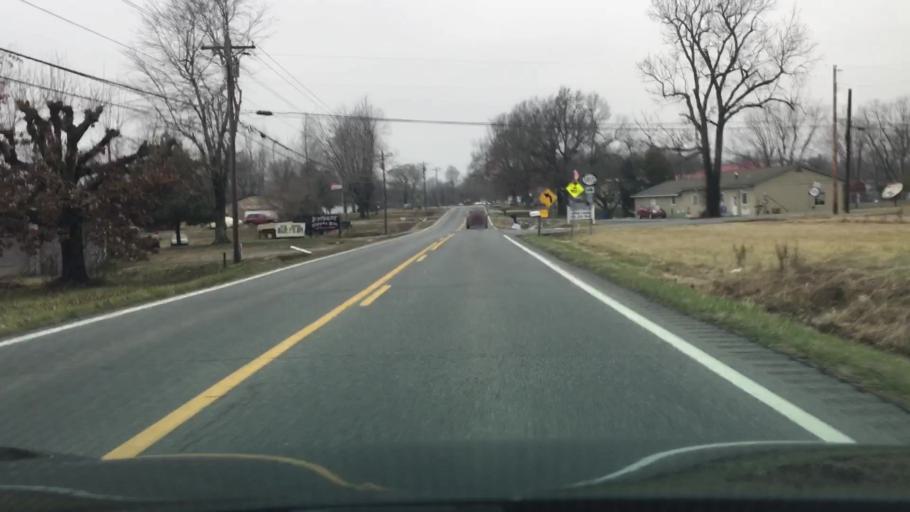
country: US
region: Kentucky
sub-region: Marshall County
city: Calvert City
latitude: 36.9728
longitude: -88.3969
